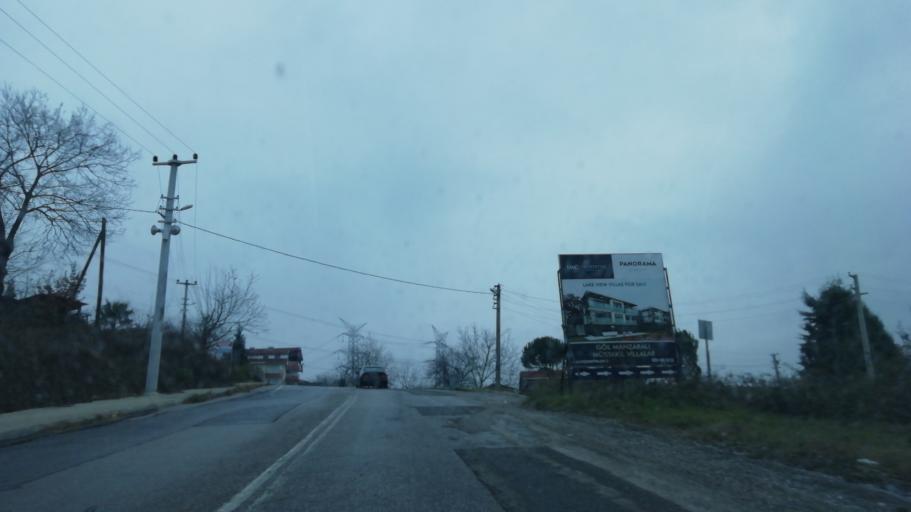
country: TR
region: Sakarya
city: Kazimpasa
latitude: 40.7428
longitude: 30.3144
